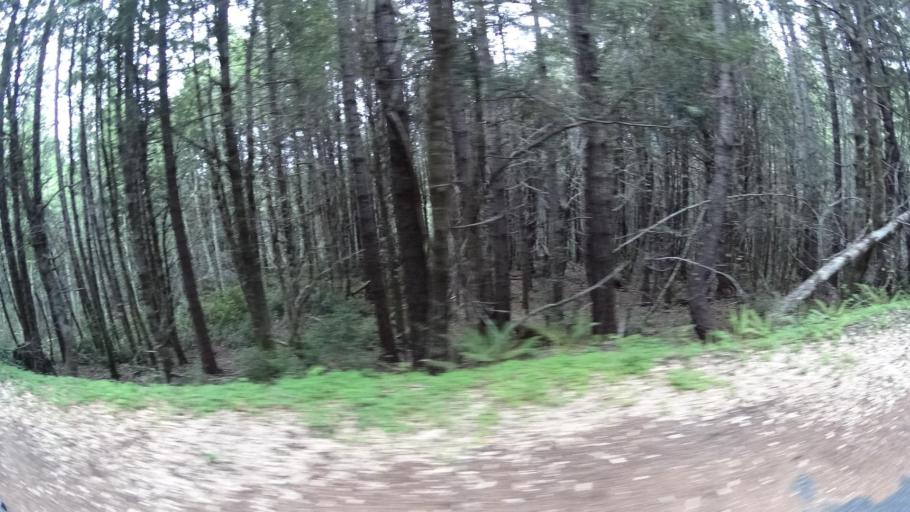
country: US
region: California
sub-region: Humboldt County
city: Willow Creek
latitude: 41.2038
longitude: -123.7753
